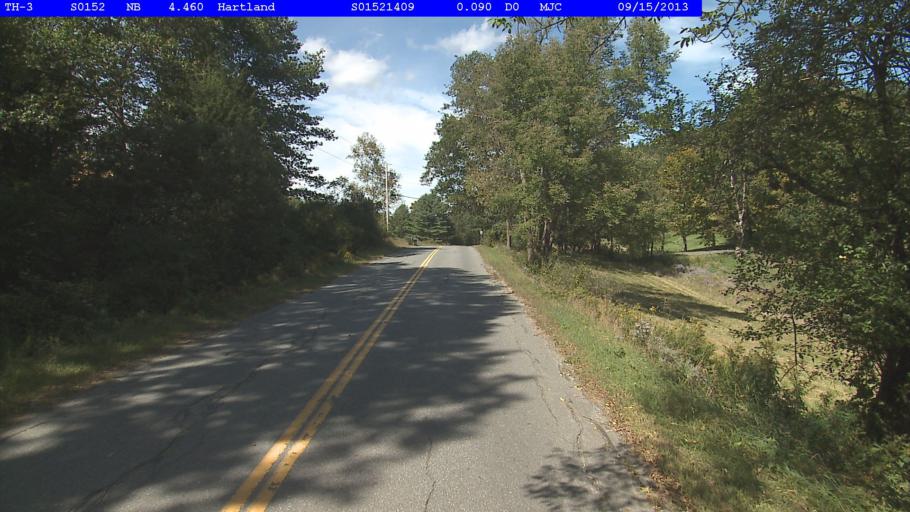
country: US
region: Vermont
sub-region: Windsor County
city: Windsor
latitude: 43.5242
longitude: -72.4346
